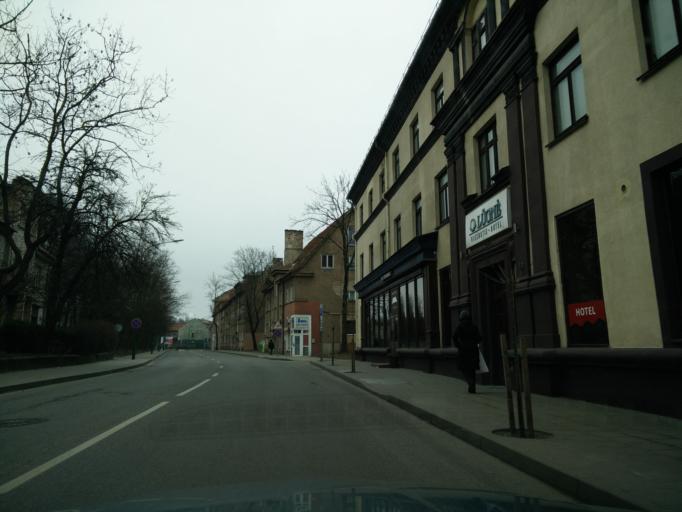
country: LT
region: Klaipedos apskritis
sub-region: Klaipeda
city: Klaipeda
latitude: 55.7045
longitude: 21.1378
